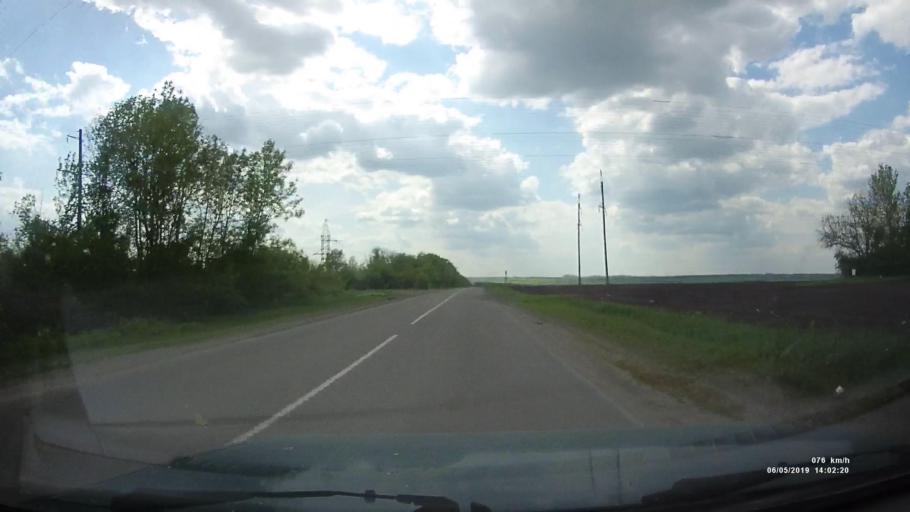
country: RU
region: Rostov
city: Shakhty
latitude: 47.6825
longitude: 40.3651
